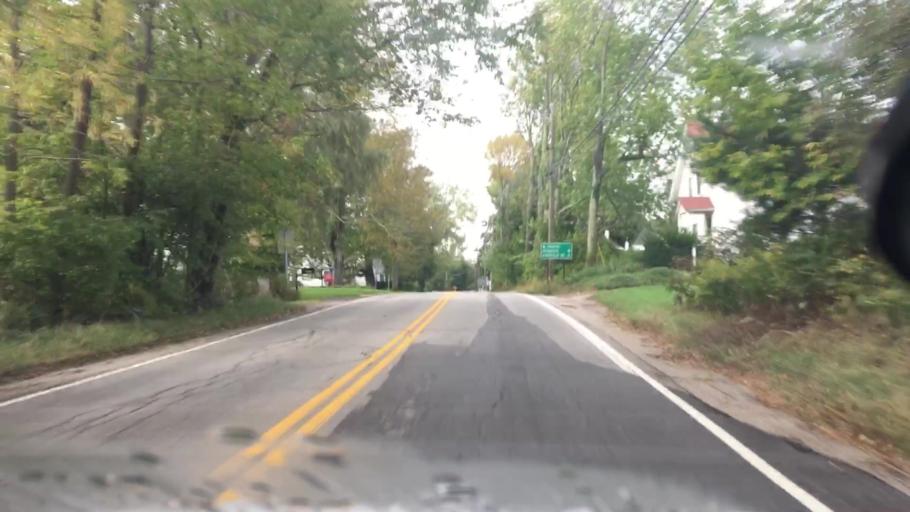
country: US
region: New Hampshire
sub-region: Carroll County
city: Wakefield
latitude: 43.5671
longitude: -71.0290
